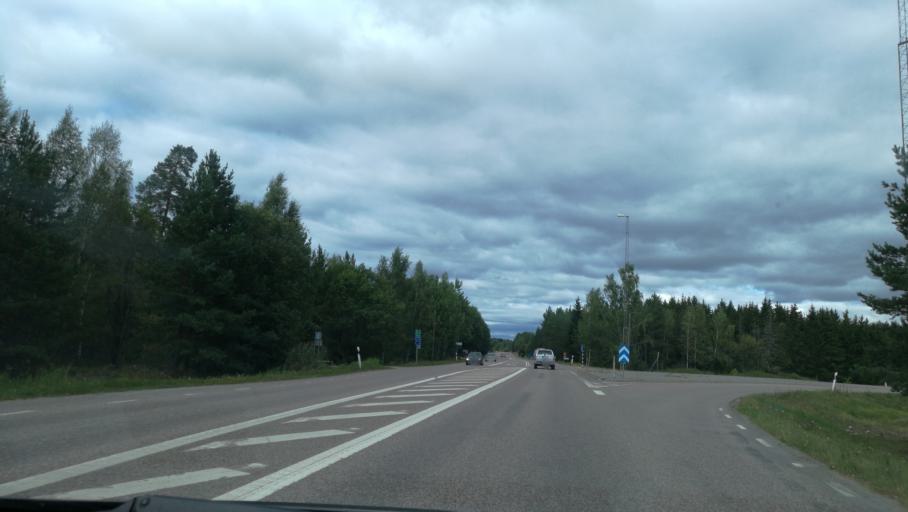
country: SE
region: Vaestmanland
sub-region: Hallstahammars Kommun
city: Kolback
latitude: 59.5656
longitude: 16.3485
